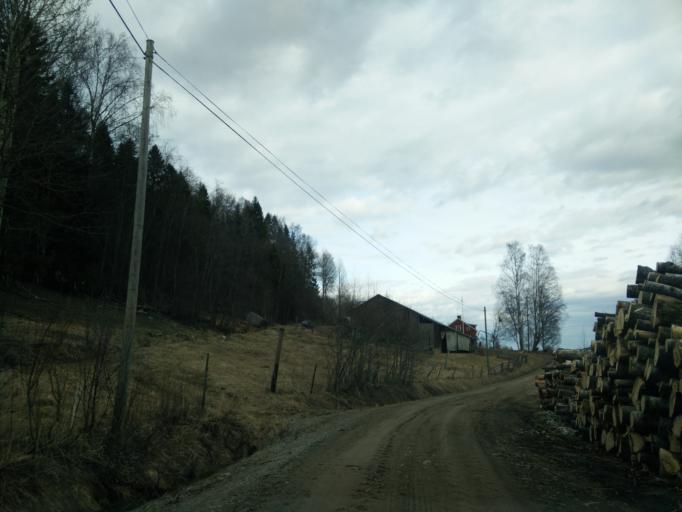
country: SE
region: Vaesternorrland
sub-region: Haernoesands Kommun
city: Haernoesand
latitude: 62.7434
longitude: 18.0578
